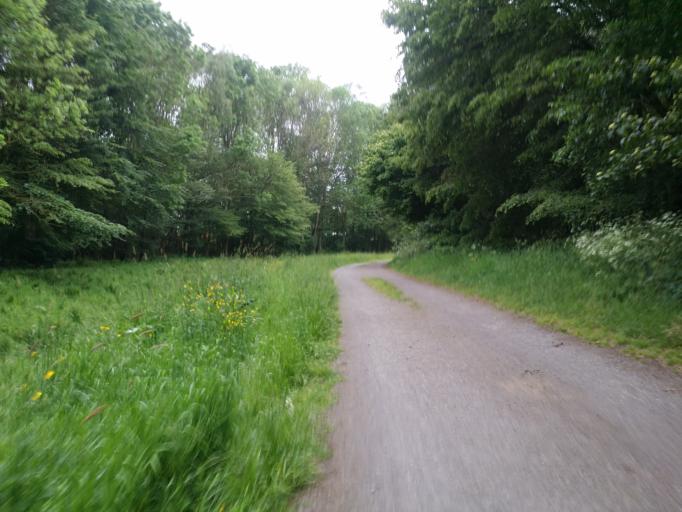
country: DE
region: Lower Saxony
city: Oldenburg
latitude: 53.1820
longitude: 8.2662
